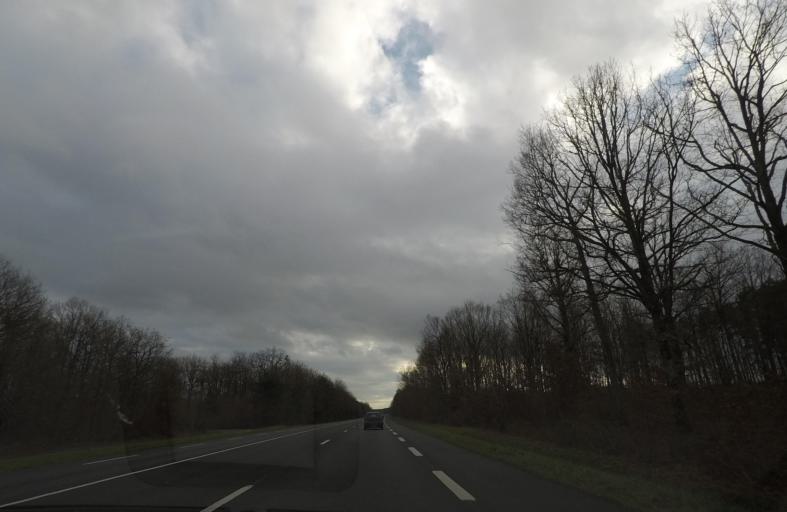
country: FR
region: Centre
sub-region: Departement du Loir-et-Cher
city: Soings-en-Sologne
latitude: 47.4540
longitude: 1.5301
